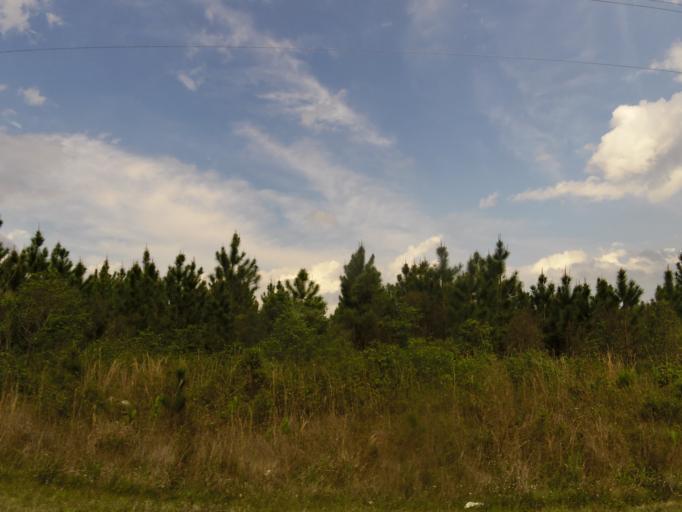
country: US
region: Georgia
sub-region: Charlton County
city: Folkston
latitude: 30.8167
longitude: -82.0704
